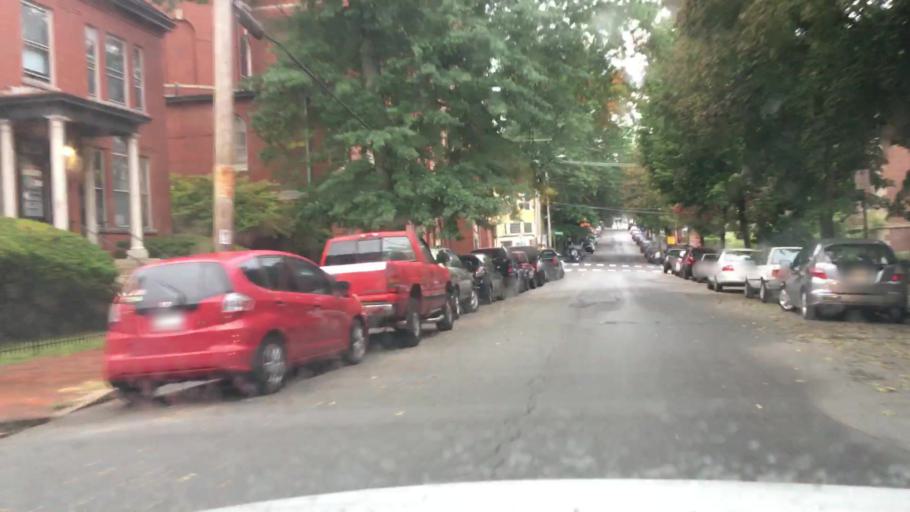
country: US
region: Maine
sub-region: Cumberland County
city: Portland
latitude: 43.6557
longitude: -70.2694
